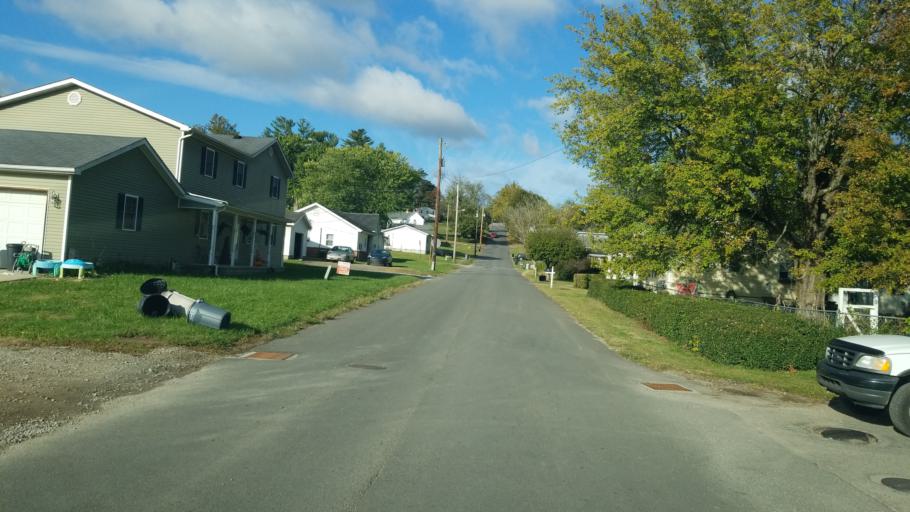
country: US
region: Ohio
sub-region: Jackson County
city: Wellston
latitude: 39.1146
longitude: -82.5369
